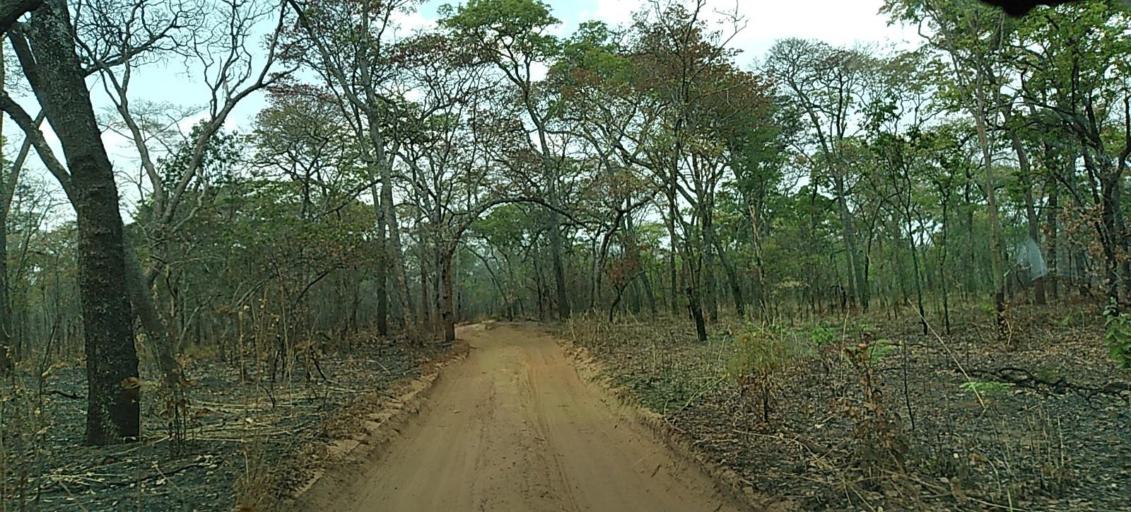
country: ZM
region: North-Western
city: Kabompo
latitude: -13.6135
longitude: 24.3729
